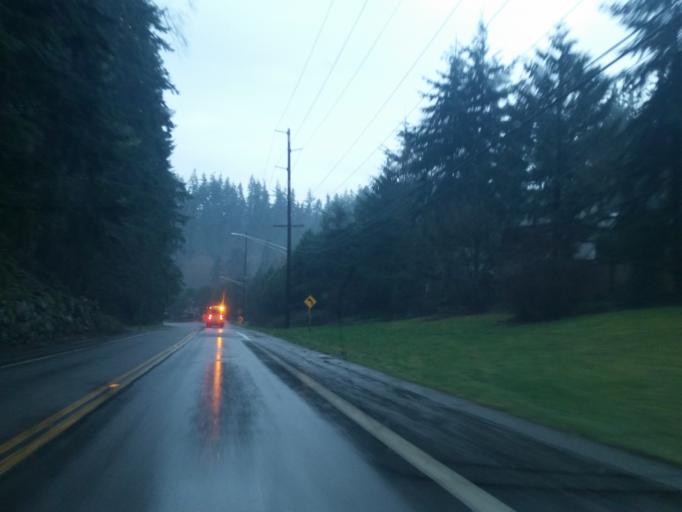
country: US
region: Washington
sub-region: Snohomish County
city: Meadowdale
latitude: 47.8756
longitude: -122.3125
